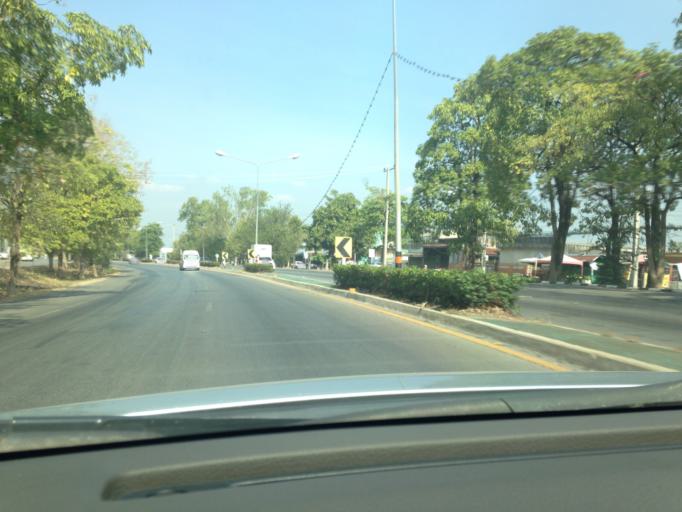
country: TH
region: Phetchabun
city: Wichian Buri
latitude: 15.5789
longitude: 101.0654
